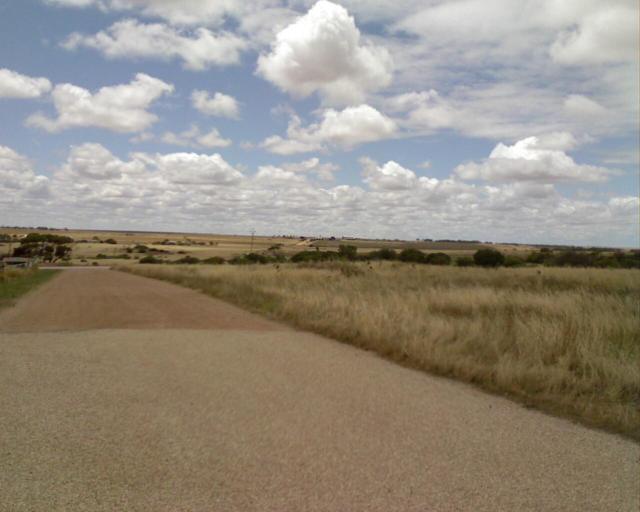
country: AU
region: South Australia
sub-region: Ceduna
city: Ceduna
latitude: -31.9297
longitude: 133.0115
